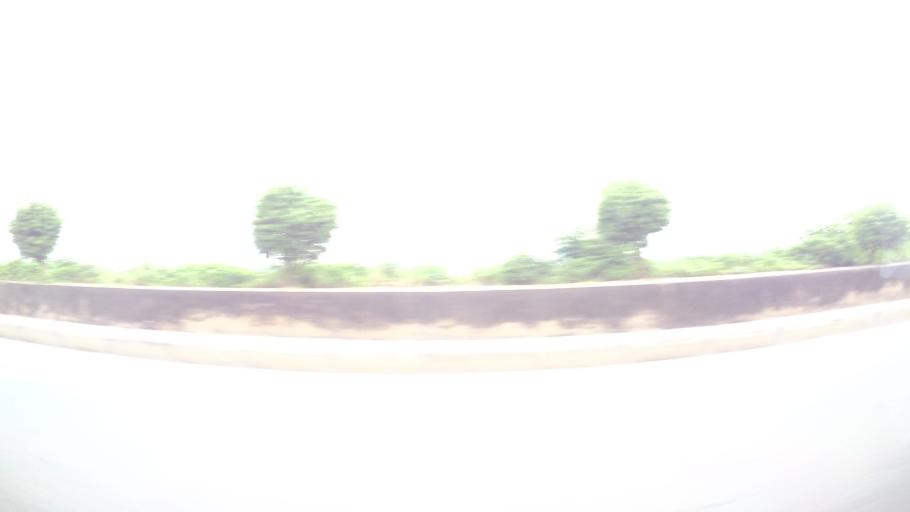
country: VN
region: Ha Noi
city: Hoan Kiem
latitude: 21.0683
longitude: 105.8761
